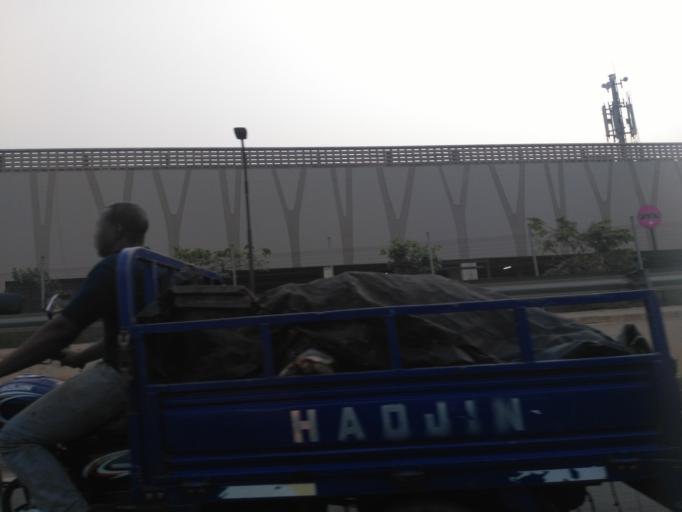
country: GH
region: Ashanti
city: Kumasi
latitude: 6.6720
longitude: -1.6075
